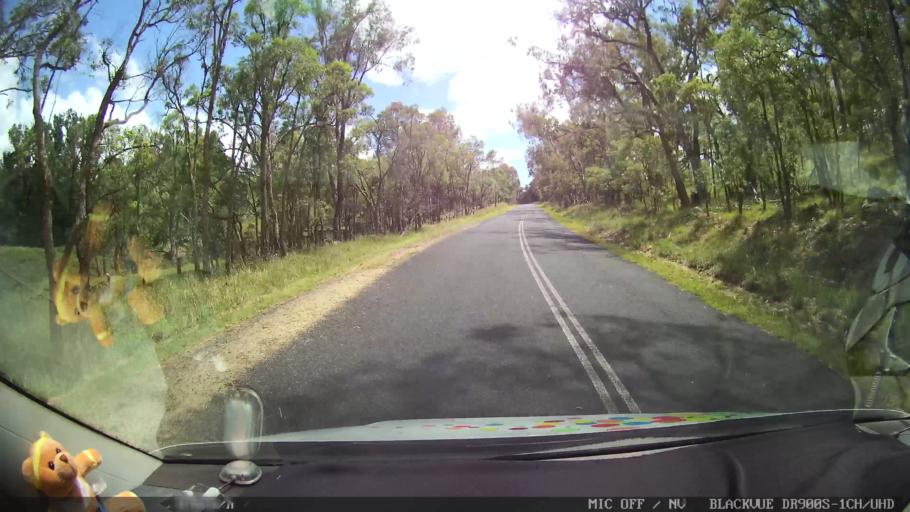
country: AU
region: New South Wales
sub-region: Glen Innes Severn
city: Glen Innes
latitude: -29.4897
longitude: 151.6825
